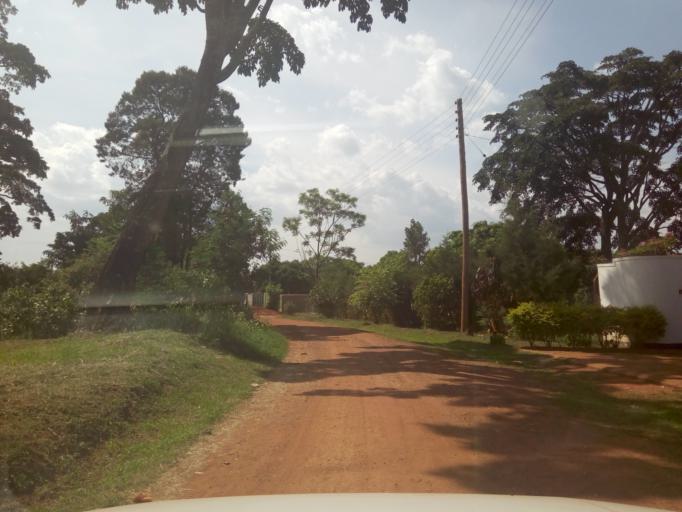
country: UG
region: Western Region
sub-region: Masindi District
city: Masindi
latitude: 1.6924
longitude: 31.7244
